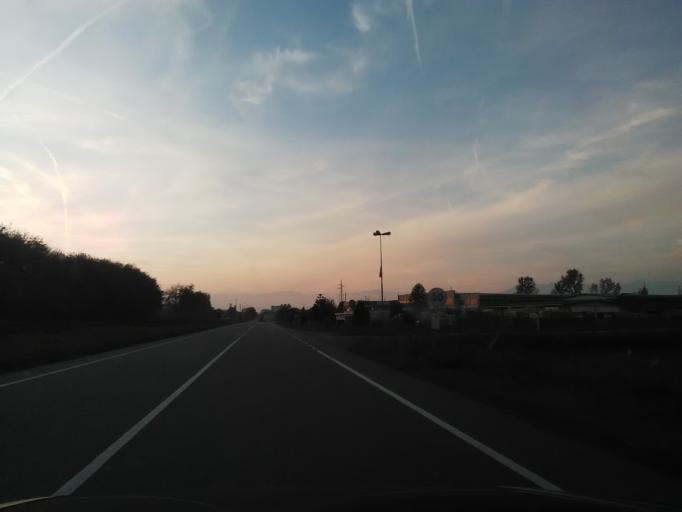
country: IT
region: Piedmont
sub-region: Provincia di Vercelli
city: Santhia
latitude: 45.3619
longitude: 8.1922
